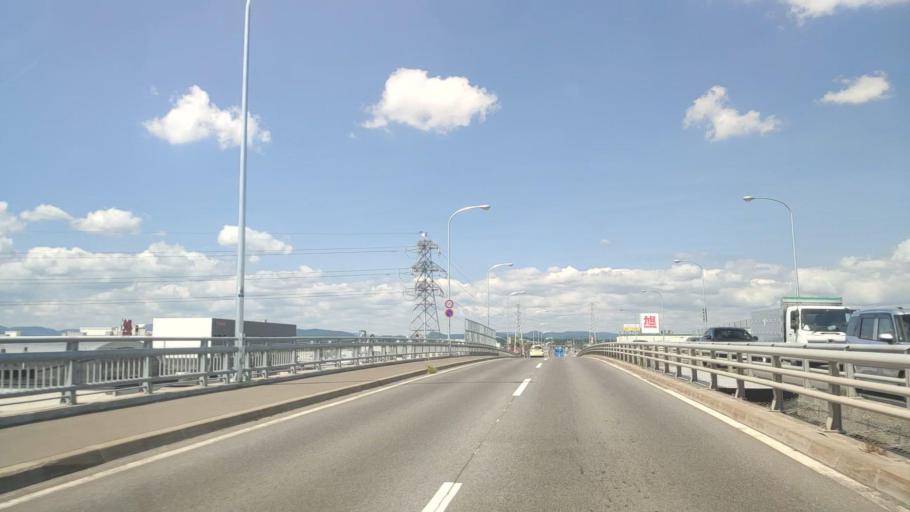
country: JP
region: Hokkaido
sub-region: Asahikawa-shi
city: Asahikawa
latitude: 43.7934
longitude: 142.4014
